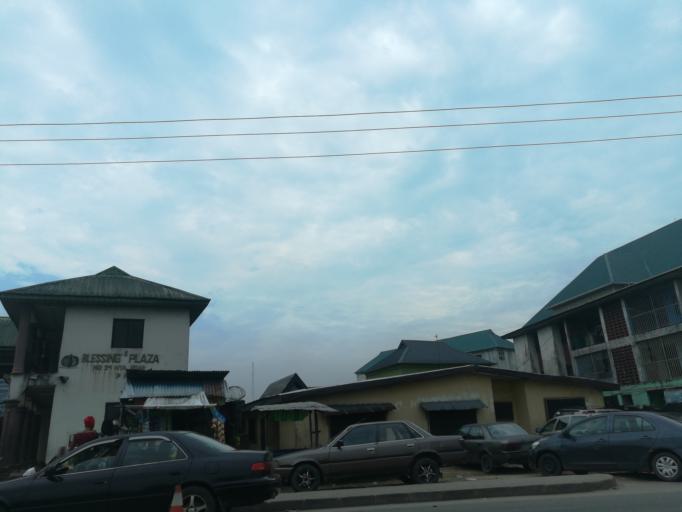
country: NG
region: Rivers
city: Port Harcourt
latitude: 4.8411
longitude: 6.9850
